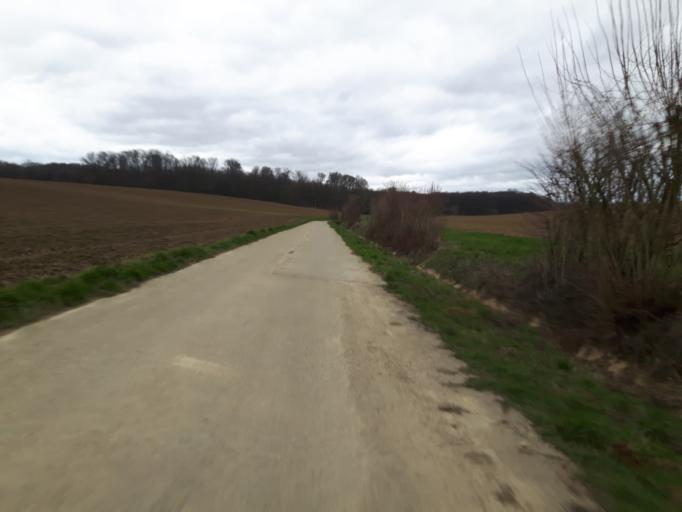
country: DE
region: Baden-Wuerttemberg
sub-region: Regierungsbezirk Stuttgart
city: Leingarten
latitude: 49.1769
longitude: 9.1029
